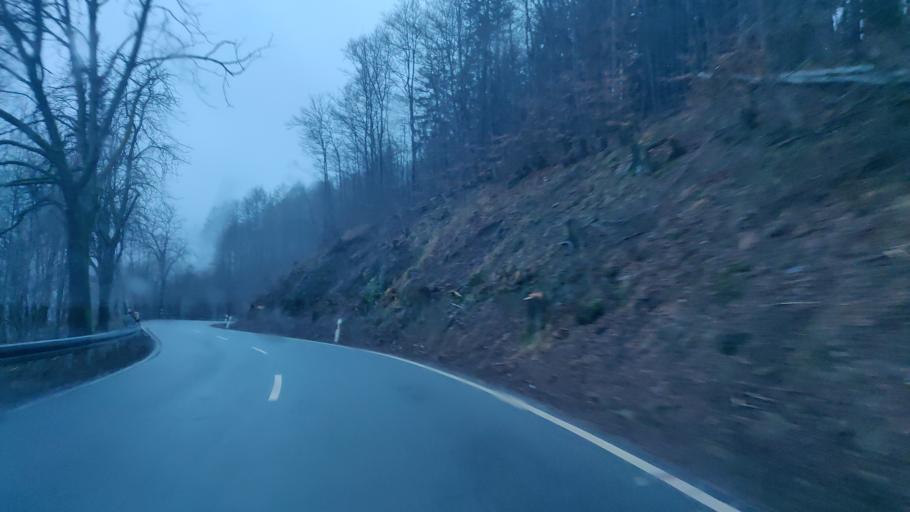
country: DE
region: Lower Saxony
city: Sankt Andreasberg
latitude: 51.6568
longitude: 10.5208
